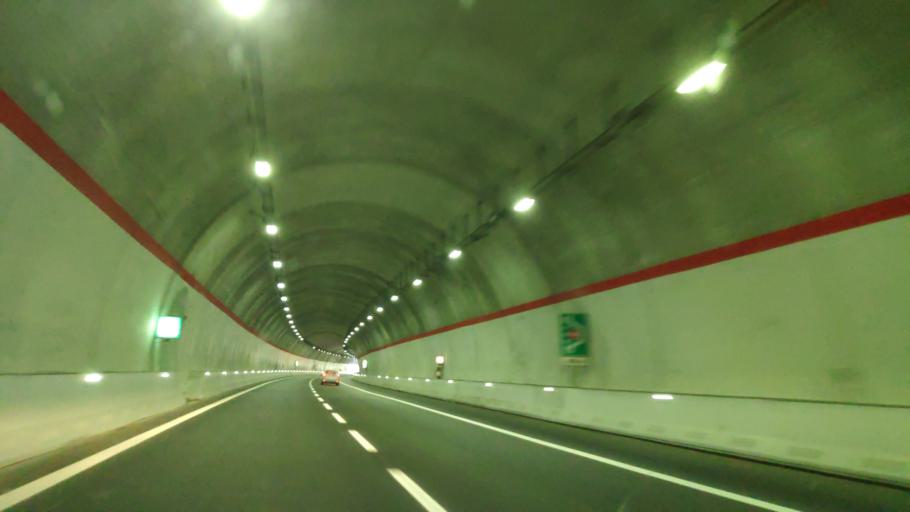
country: IT
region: Basilicate
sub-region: Provincia di Potenza
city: Lagonegro
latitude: 40.1124
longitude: 15.7891
